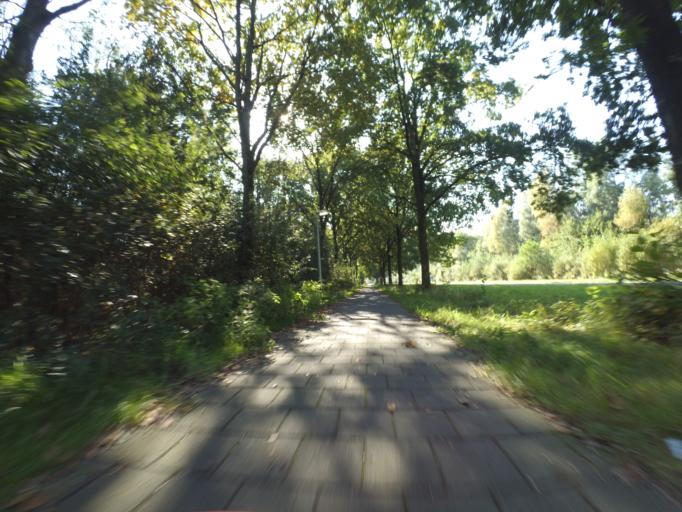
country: NL
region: Flevoland
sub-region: Gemeente Zeewolde
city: Zeewolde
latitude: 52.3148
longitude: 5.5332
